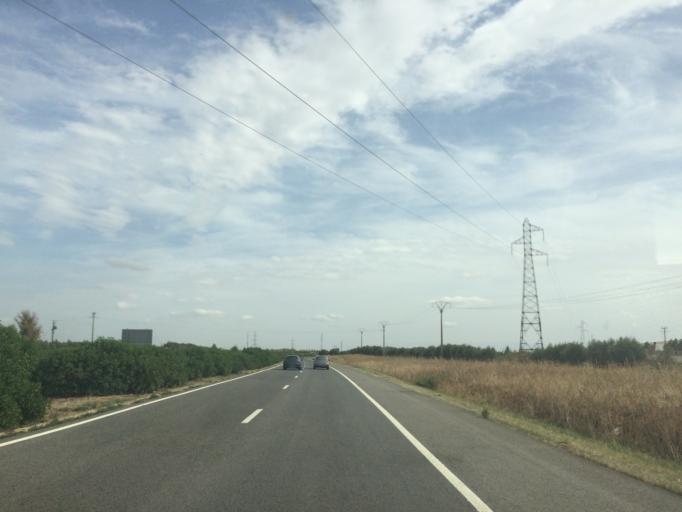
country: MA
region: Meknes-Tafilalet
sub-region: Meknes
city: Meknes
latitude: 33.8290
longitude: -5.5258
